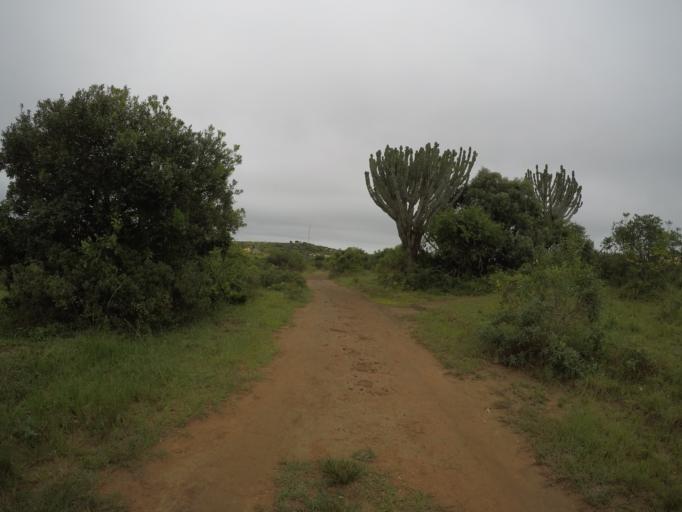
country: ZA
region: KwaZulu-Natal
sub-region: uThungulu District Municipality
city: Empangeni
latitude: -28.6074
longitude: 31.8435
